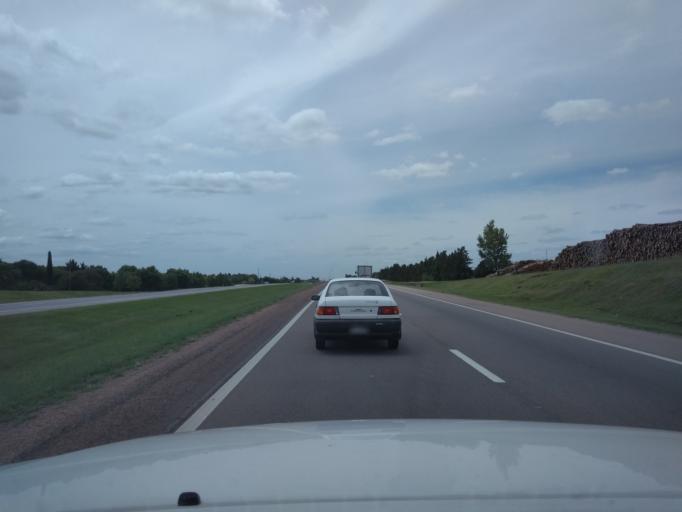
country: UY
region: Canelones
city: La Paz
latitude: -34.7420
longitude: -56.2517
